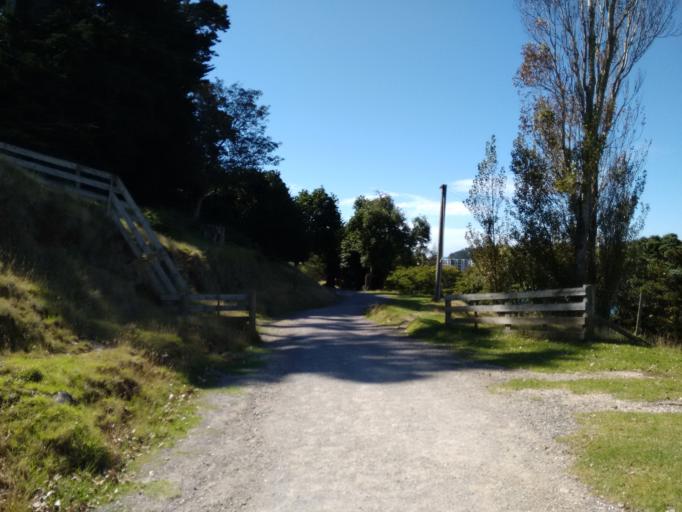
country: NZ
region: Bay of Plenty
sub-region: Tauranga City
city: Tauranga
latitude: -37.6346
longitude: 176.1727
